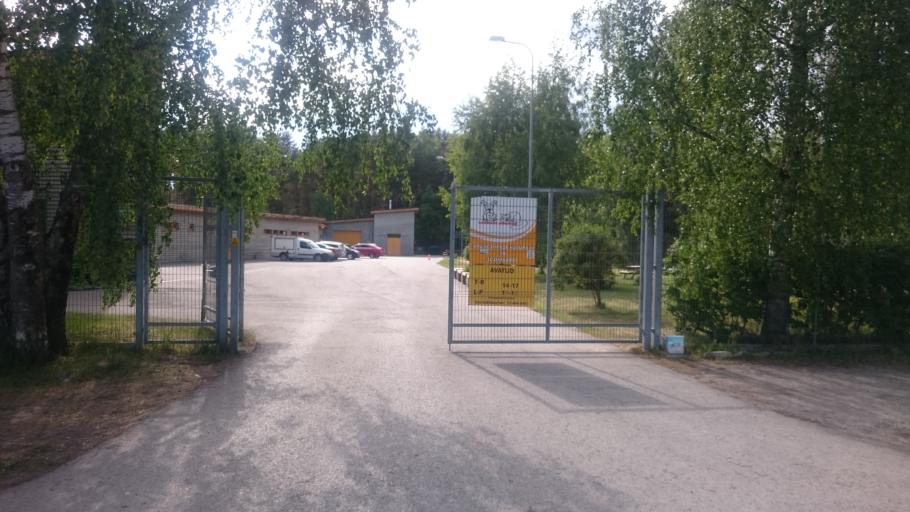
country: EE
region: Harju
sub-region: Tallinna linn
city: Tallinn
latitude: 59.3722
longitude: 24.7430
